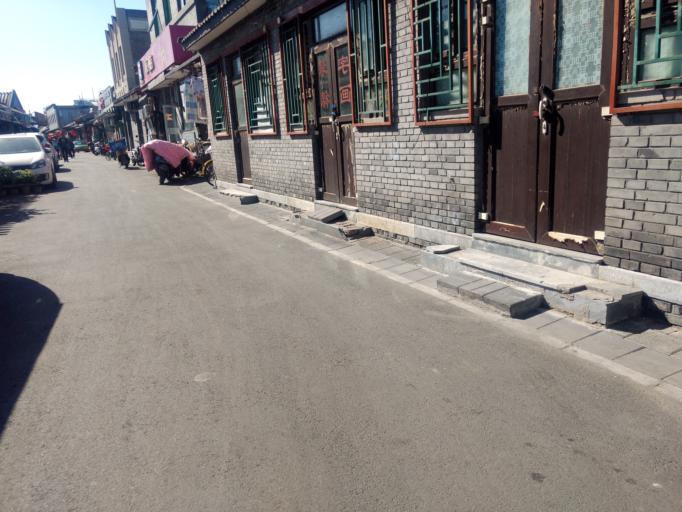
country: CN
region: Beijing
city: Beijing
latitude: 39.8922
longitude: 116.3833
